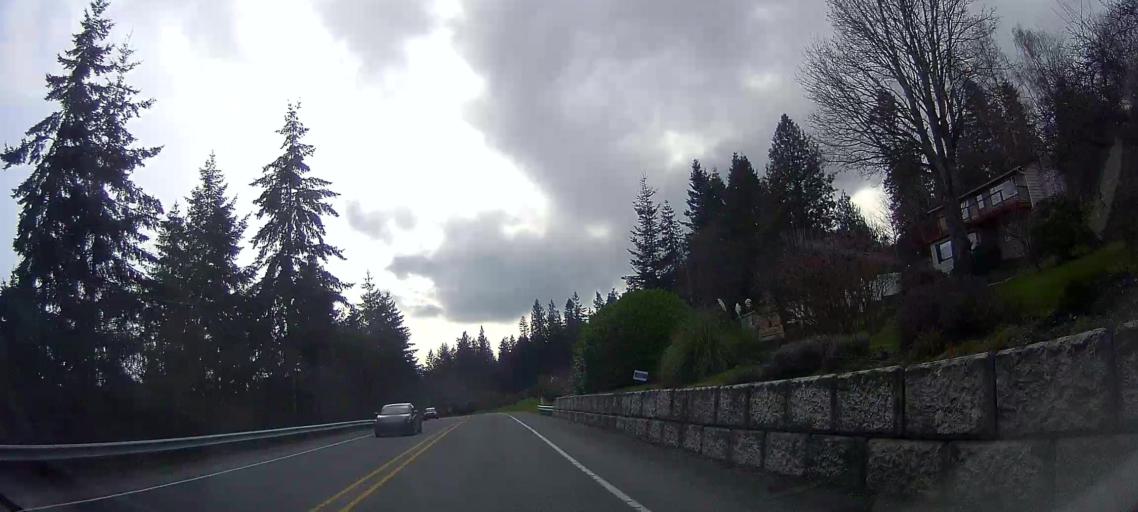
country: US
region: Washington
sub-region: Island County
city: Camano
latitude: 48.1855
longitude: -122.4807
